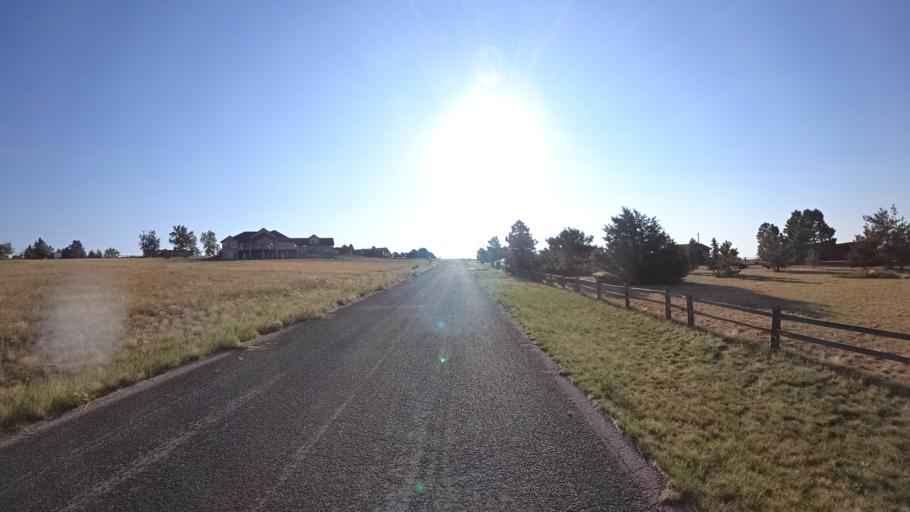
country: US
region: Colorado
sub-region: El Paso County
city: Black Forest
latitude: 38.9385
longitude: -104.7720
